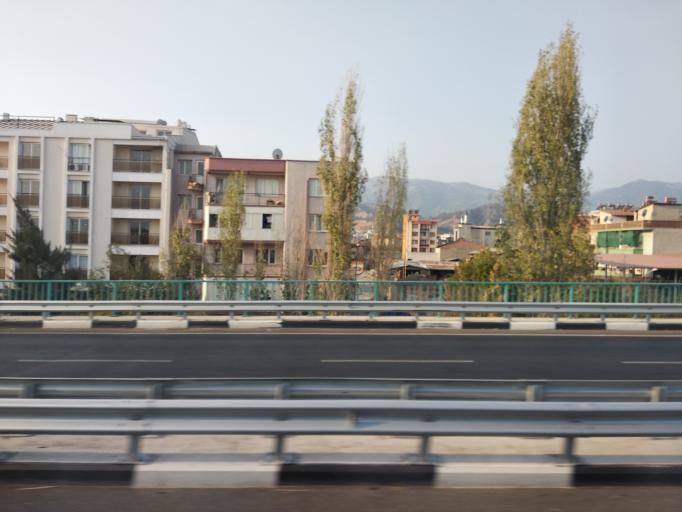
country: TR
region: Manisa
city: Salihli
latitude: 38.4903
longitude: 28.1429
